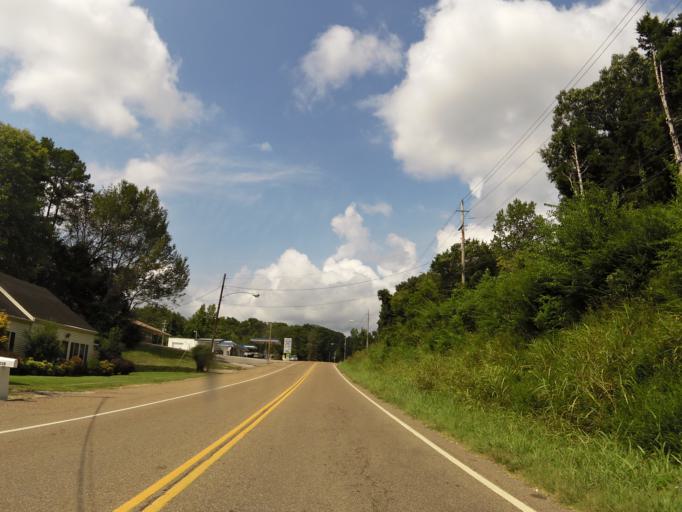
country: US
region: Tennessee
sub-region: Perry County
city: Linden
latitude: 35.6175
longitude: -87.8451
